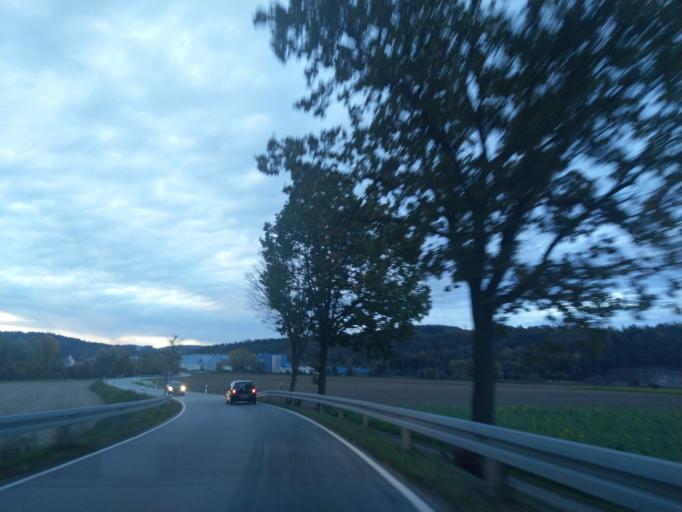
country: DE
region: Bavaria
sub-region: Lower Bavaria
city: Niederalteich
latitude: 48.7850
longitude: 13.0200
